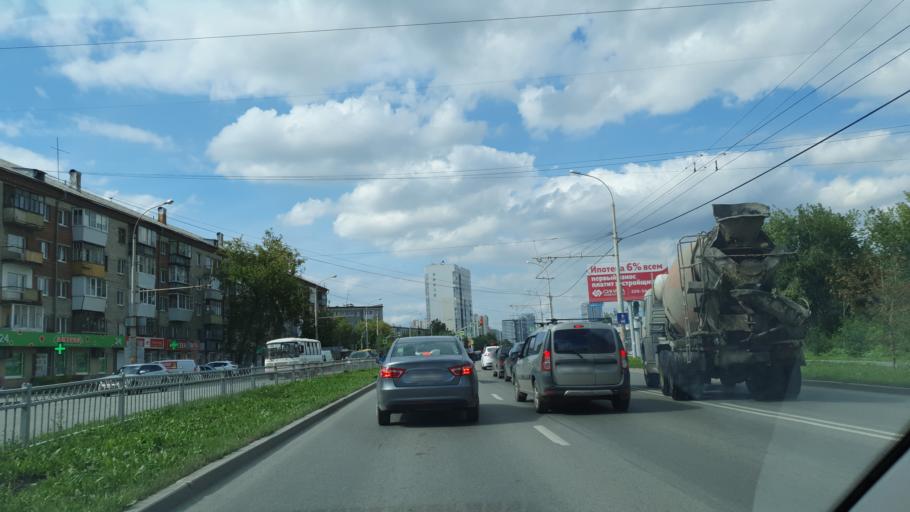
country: RU
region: Sverdlovsk
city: Yekaterinburg
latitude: 56.7861
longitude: 60.6493
